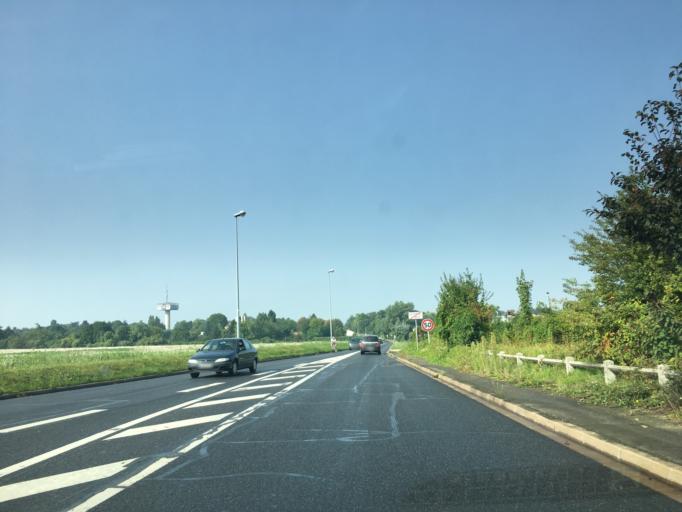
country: FR
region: Ile-de-France
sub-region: Departement du Val-de-Marne
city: La Queue-en-Brie
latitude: 48.7817
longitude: 2.5681
